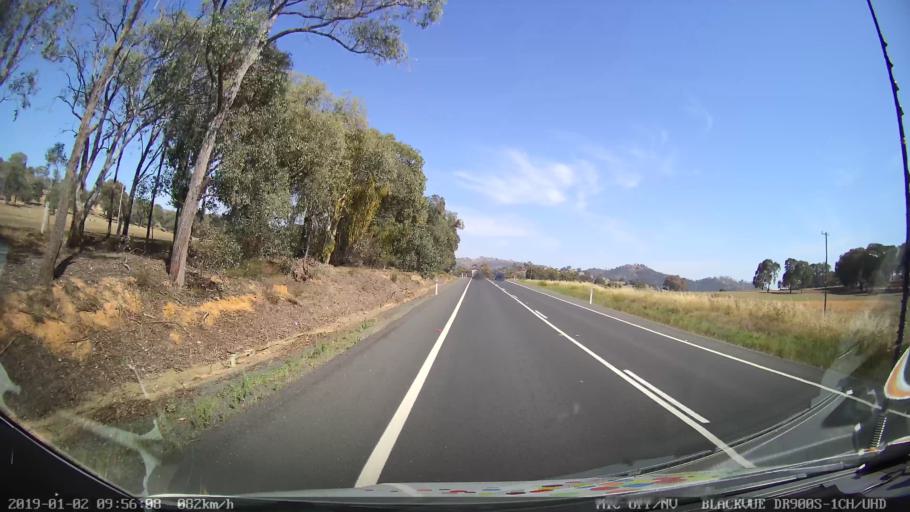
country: AU
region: New South Wales
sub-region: Tumut Shire
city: Tumut
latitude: -35.2179
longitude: 148.1798
